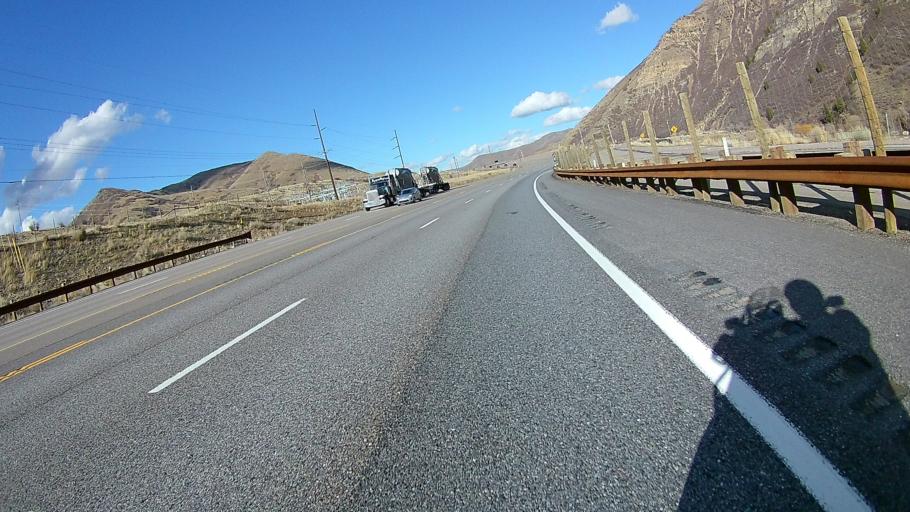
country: US
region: Utah
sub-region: Wasatch County
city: Midway
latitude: 40.3981
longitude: -111.5401
